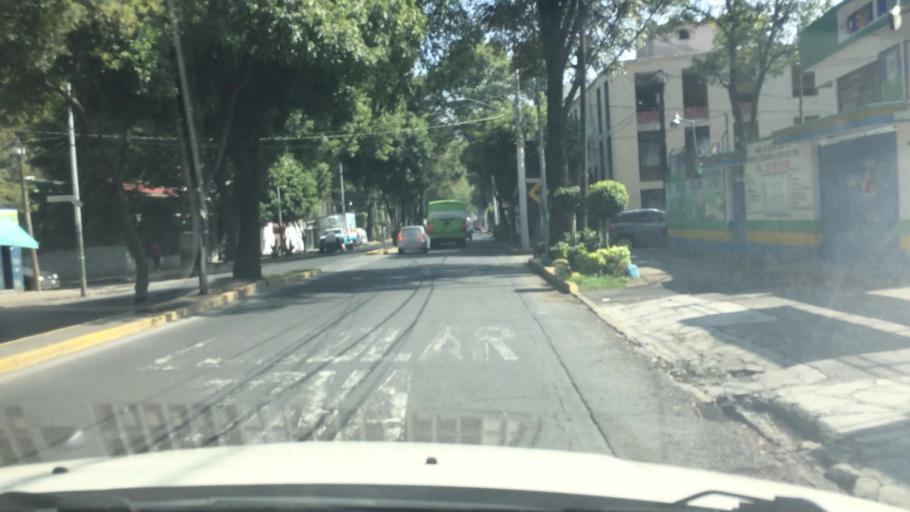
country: MX
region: Mexico City
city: Tlalpan
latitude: 19.2838
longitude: -99.1644
